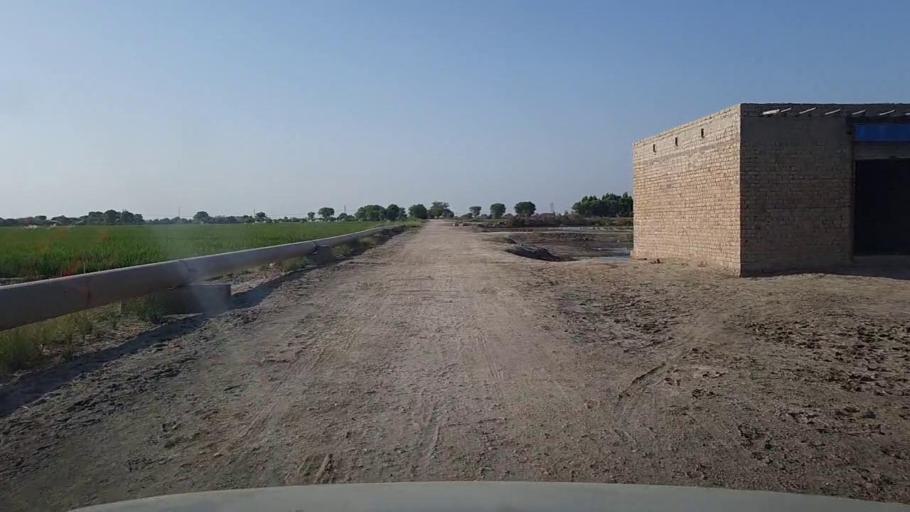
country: PK
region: Sindh
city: Kandhkot
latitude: 28.2857
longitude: 69.3337
